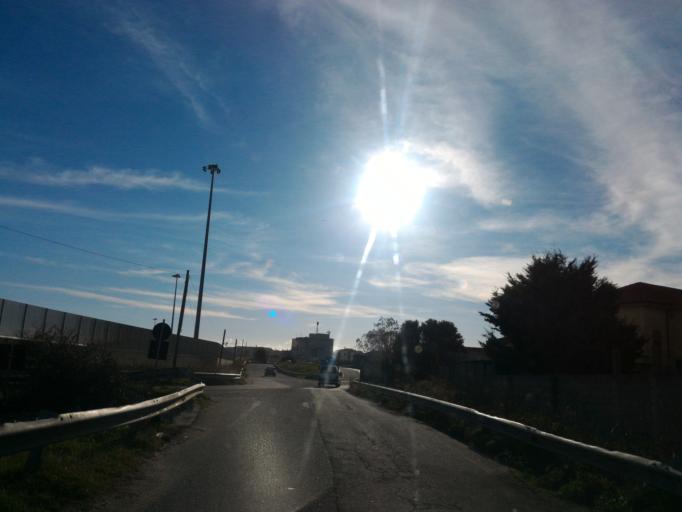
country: IT
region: Calabria
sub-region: Provincia di Crotone
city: Crotone
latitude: 39.0881
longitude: 17.1176
